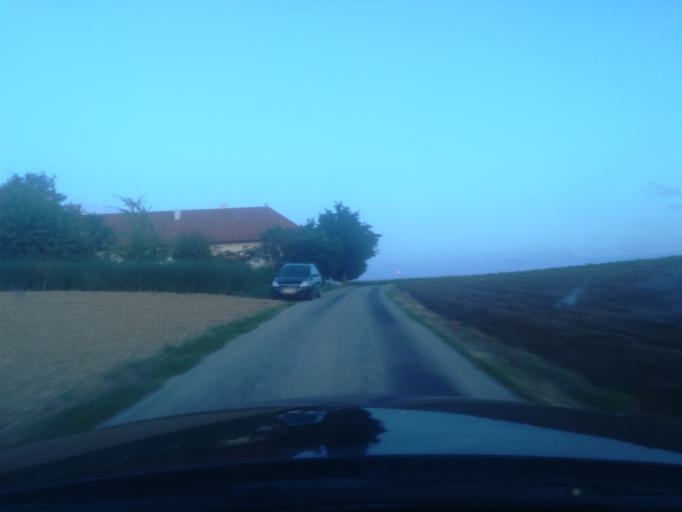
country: AT
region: Upper Austria
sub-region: Wels-Land
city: Thalheim bei Wels
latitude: 48.1556
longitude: 14.0564
